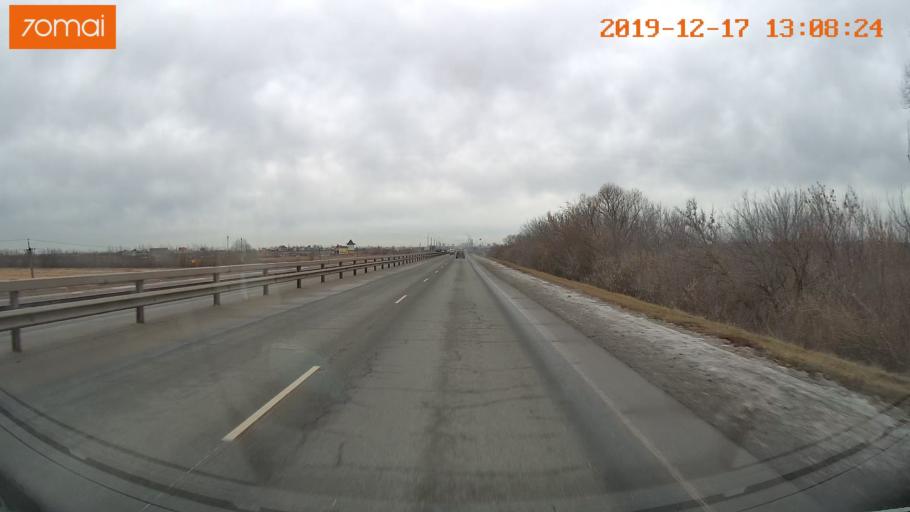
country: RU
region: Rjazan
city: Polyany
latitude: 54.6737
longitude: 39.8261
